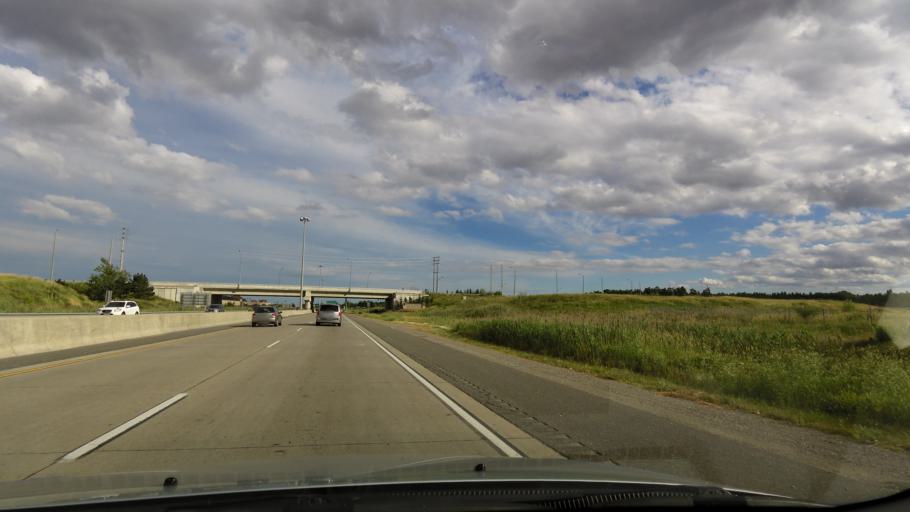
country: CA
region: Ontario
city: Brampton
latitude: 43.7497
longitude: -79.7899
